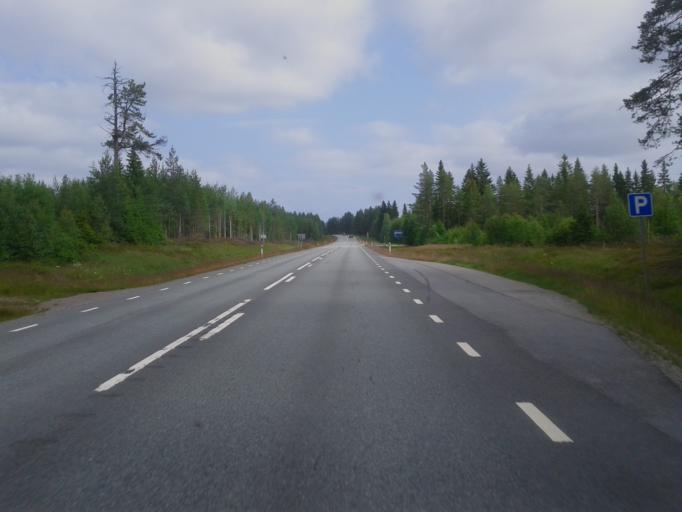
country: SE
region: Vaesterbotten
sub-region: Skelleftea Kommun
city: Burea
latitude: 64.3452
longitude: 21.2856
